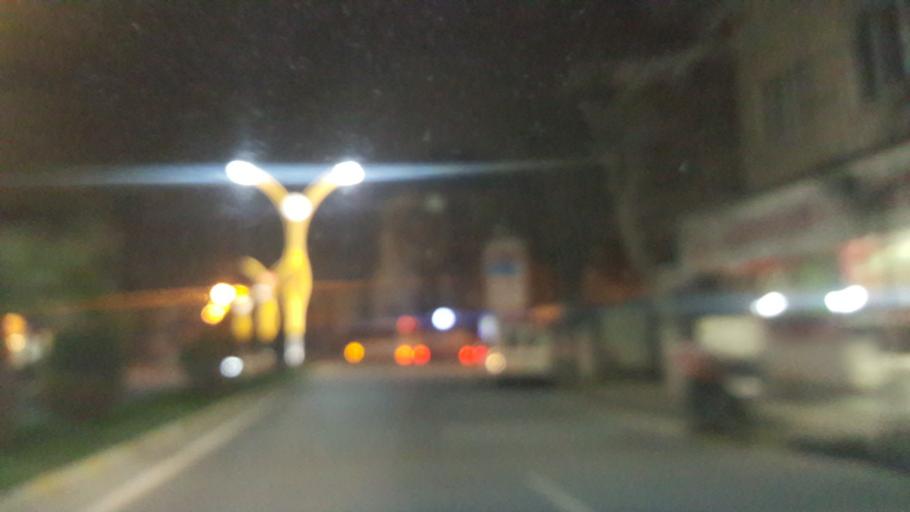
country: TR
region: Kocaeli
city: Darica
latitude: 40.7818
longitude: 29.3974
